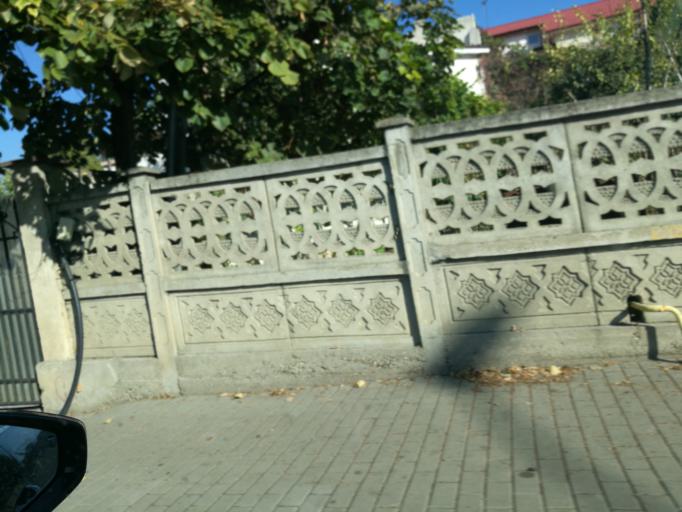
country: RO
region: Iasi
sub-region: Municipiul Iasi
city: Iasi
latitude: 47.1723
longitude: 27.5641
